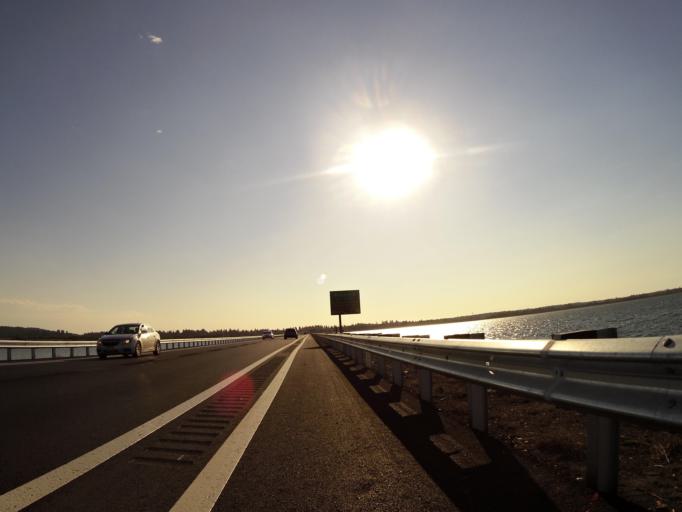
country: US
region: Oregon
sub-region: Clatsop County
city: Warrenton
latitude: 46.1709
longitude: -123.8785
